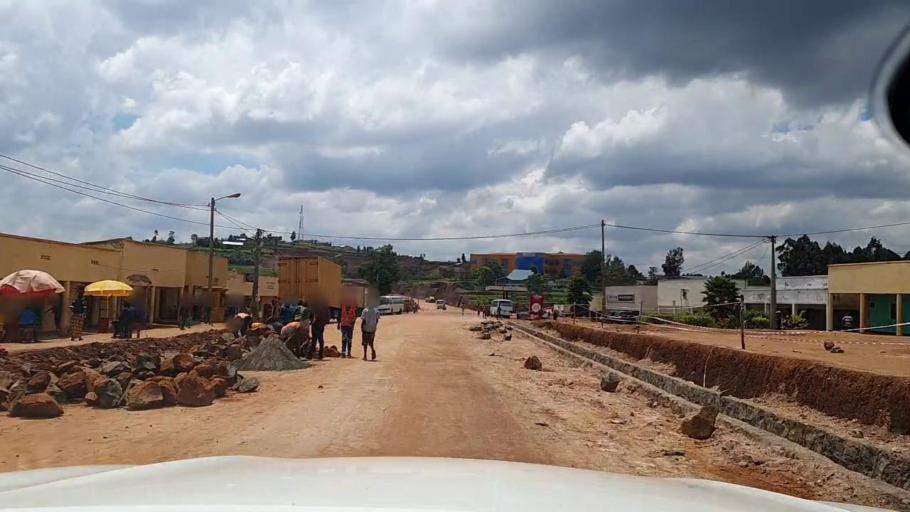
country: RW
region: Southern Province
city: Butare
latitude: -2.6961
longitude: 29.5697
